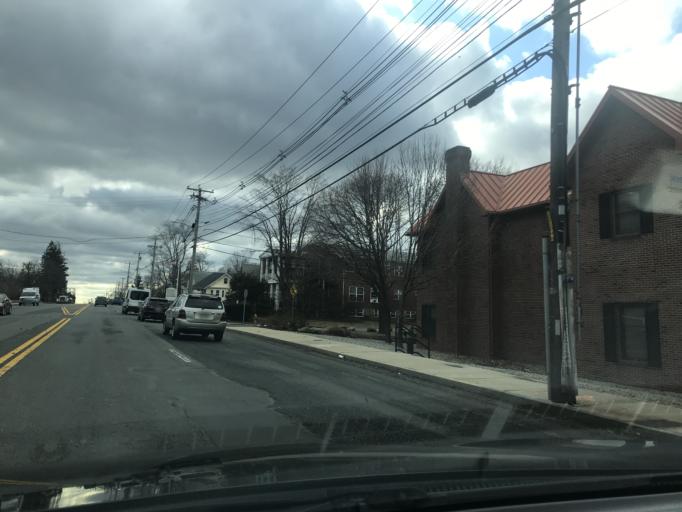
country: US
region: Massachusetts
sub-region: Norfolk County
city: Weymouth
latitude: 42.1763
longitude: -70.9554
